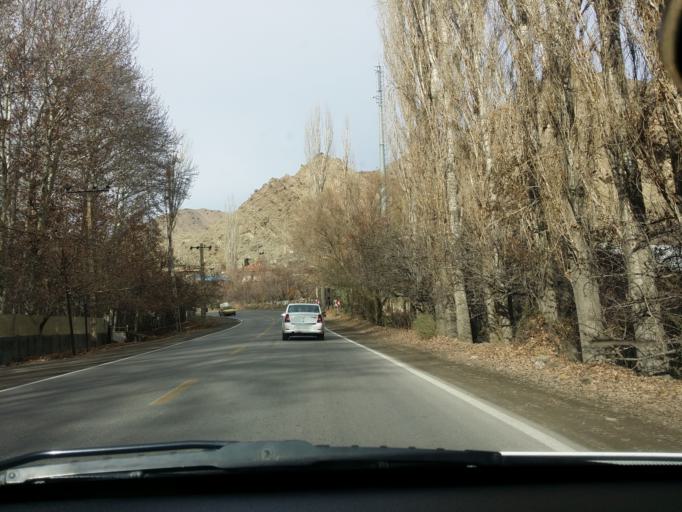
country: IR
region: Tehran
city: Tajrish
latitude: 36.0288
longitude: 51.2388
